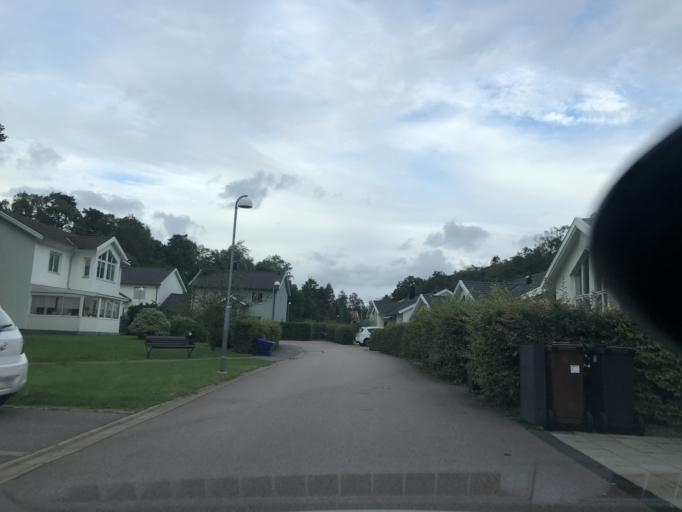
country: SE
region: Vaestra Goetaland
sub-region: Goteborg
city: Goeteborg
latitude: 57.7505
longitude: 11.9591
